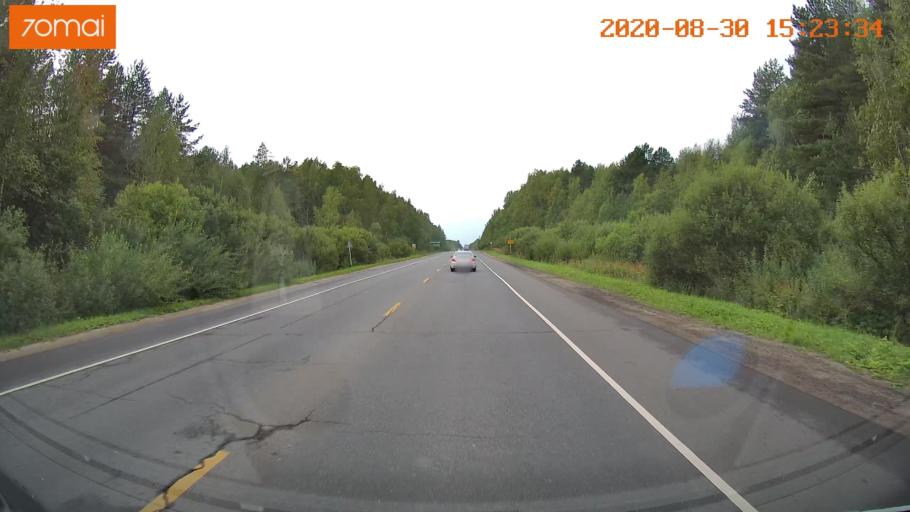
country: RU
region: Ivanovo
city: Rodniki
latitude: 57.0881
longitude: 41.7016
